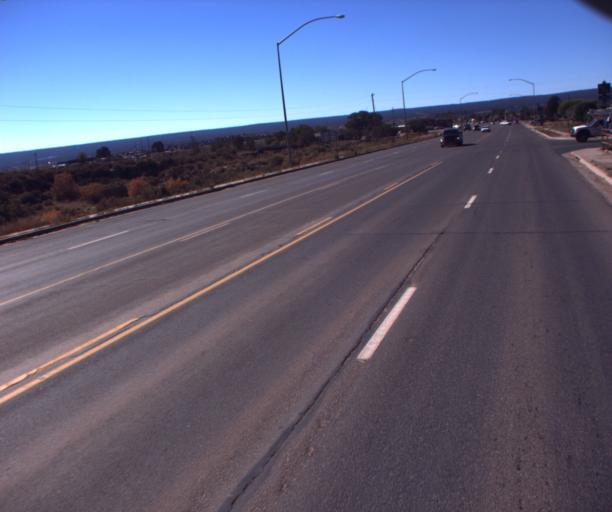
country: US
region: Arizona
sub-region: Apache County
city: Window Rock
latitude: 35.6633
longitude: -109.0515
